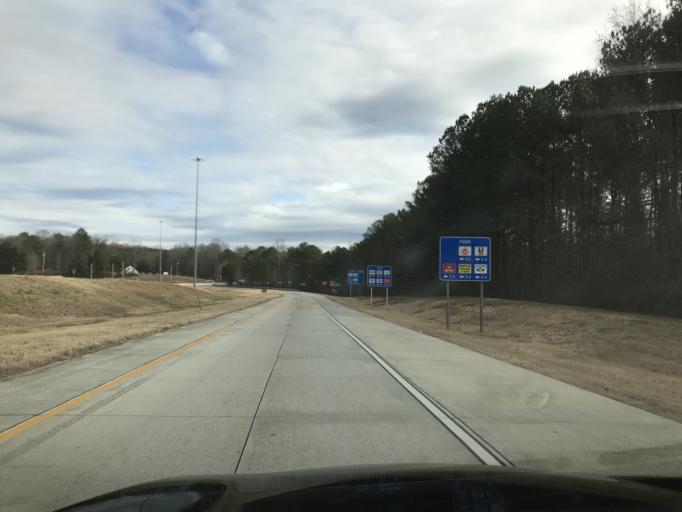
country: US
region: Georgia
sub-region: Haralson County
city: Bremen
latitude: 33.6846
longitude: -85.1544
